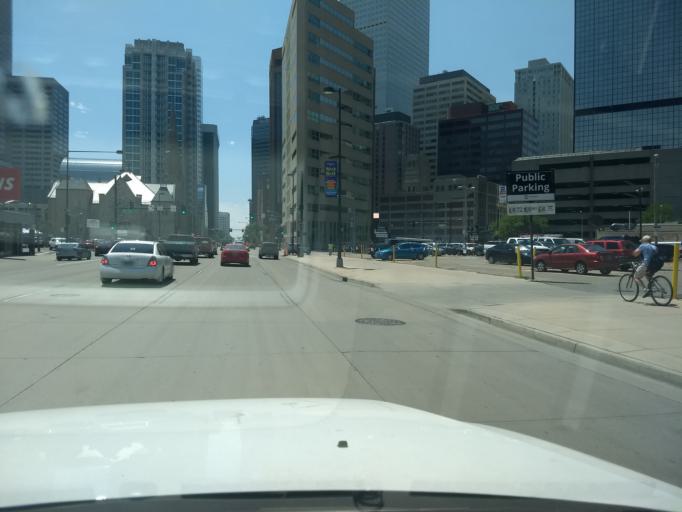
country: US
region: Colorado
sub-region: Denver County
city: Denver
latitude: 39.7469
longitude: -104.9874
